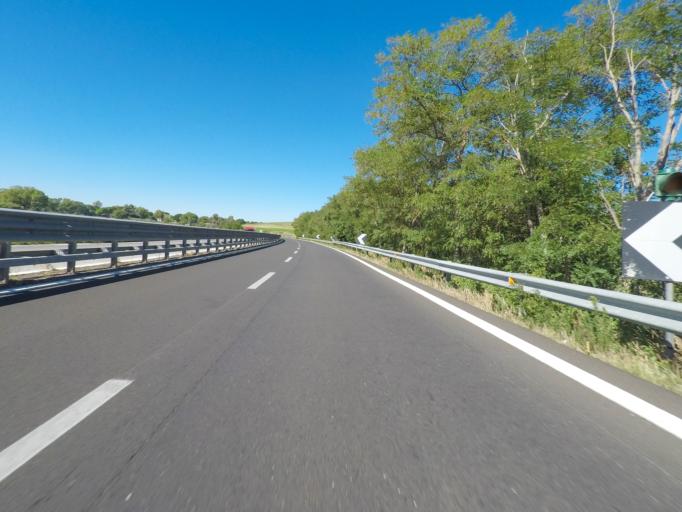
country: IT
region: Latium
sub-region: Provincia di Viterbo
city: Montalto di Castro
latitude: 42.3164
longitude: 11.6537
